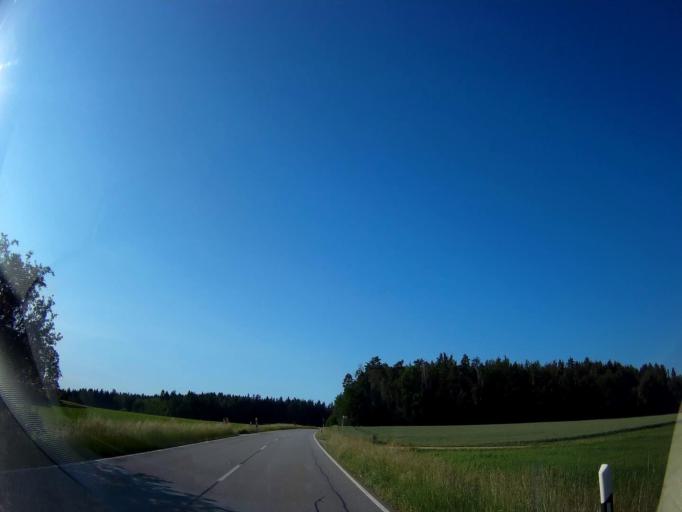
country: DE
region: Bavaria
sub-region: Lower Bavaria
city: Malgersdorf
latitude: 48.5109
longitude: 12.7412
